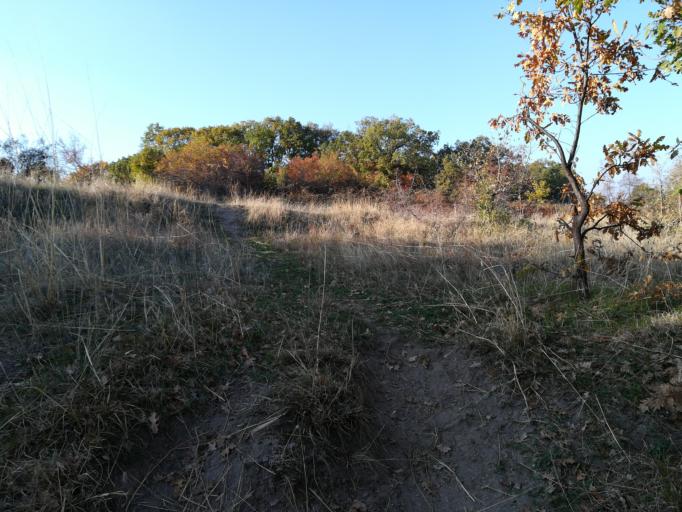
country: BG
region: Khaskovo
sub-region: Obshtina Mineralni Bani
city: Mineralni Bani
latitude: 41.9833
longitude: 25.2358
